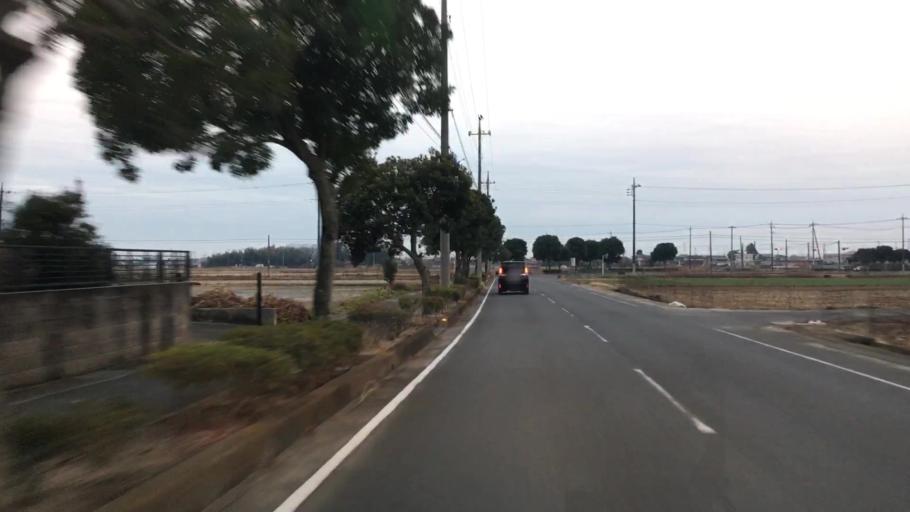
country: JP
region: Gunma
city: Ota
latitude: 36.3131
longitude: 139.3632
